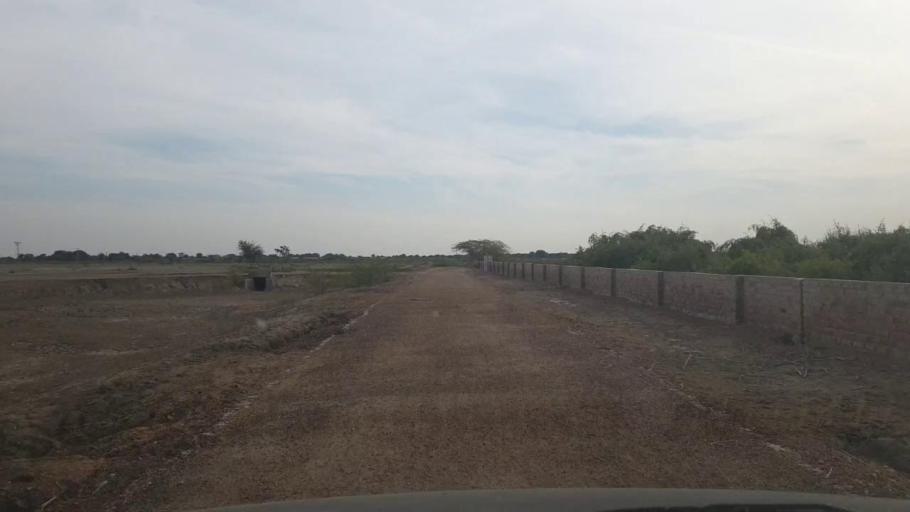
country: PK
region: Sindh
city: Kunri
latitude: 25.2970
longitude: 69.5736
